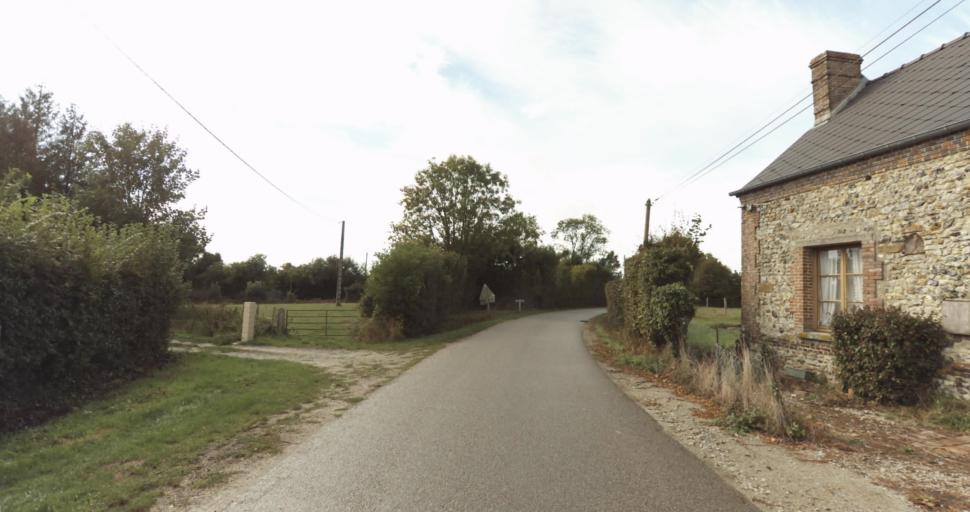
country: FR
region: Lower Normandy
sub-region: Departement de l'Orne
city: Sainte-Gauburge-Sainte-Colombe
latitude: 48.6828
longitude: 0.3888
